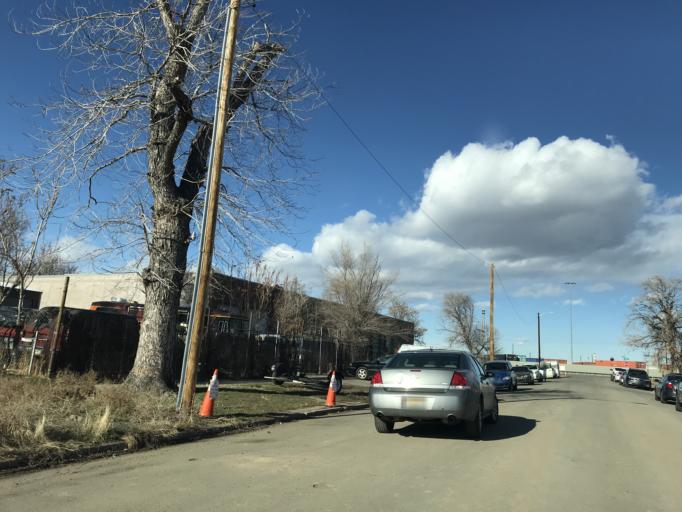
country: US
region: Colorado
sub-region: Denver County
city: Denver
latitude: 39.7717
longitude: -104.9647
